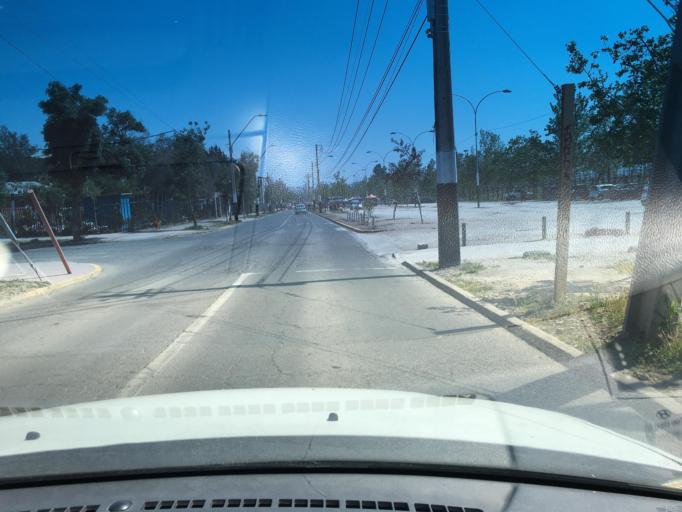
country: CL
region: Santiago Metropolitan
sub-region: Provincia de Santiago
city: Villa Presidente Frei, Nunoa, Santiago, Chile
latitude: -33.5165
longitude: -70.5518
